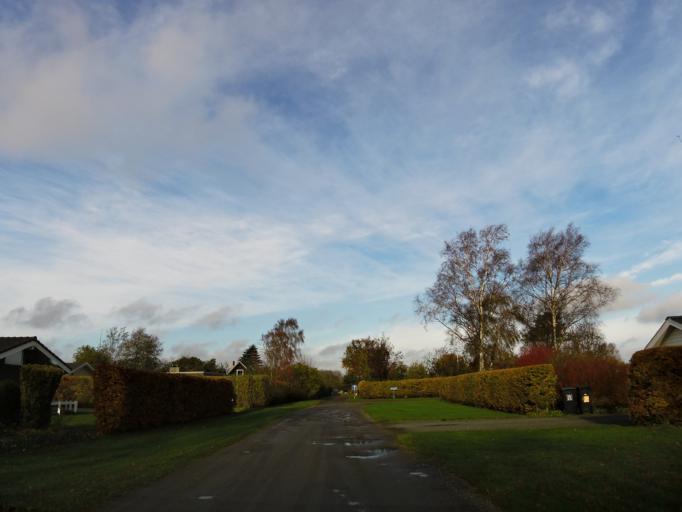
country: DK
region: Central Jutland
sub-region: Arhus Kommune
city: Malling
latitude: 55.9578
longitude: 10.2621
